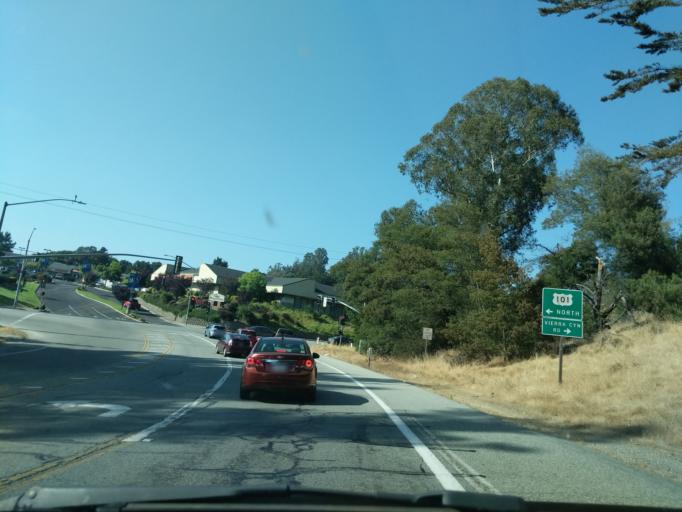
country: US
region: California
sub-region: Monterey County
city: Prunedale
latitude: 36.7913
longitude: -121.6650
